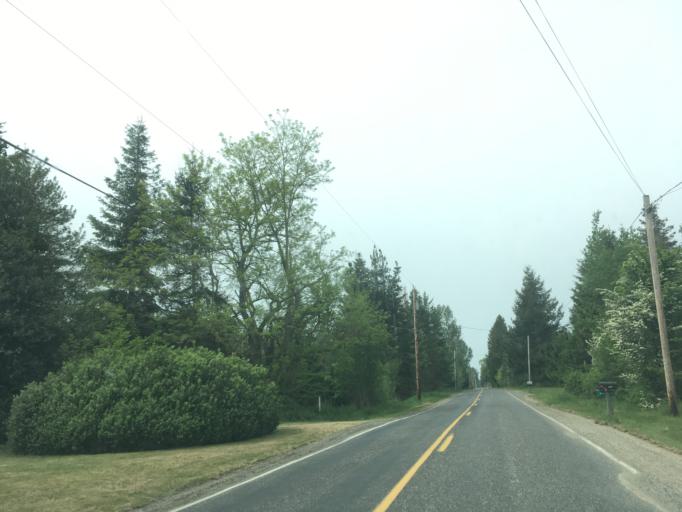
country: US
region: Washington
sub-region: Whatcom County
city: Geneva
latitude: 48.8188
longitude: -122.4076
